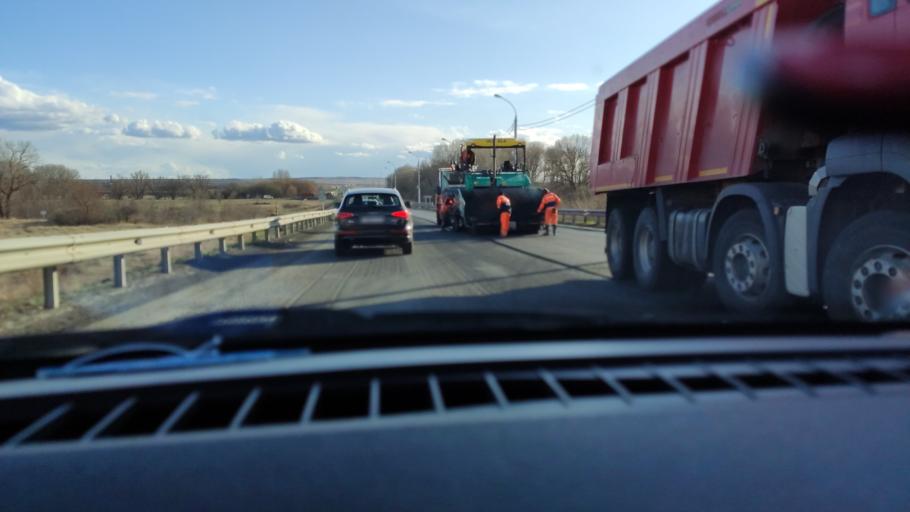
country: RU
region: Saratov
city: Yelshanka
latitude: 51.8240
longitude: 46.2195
